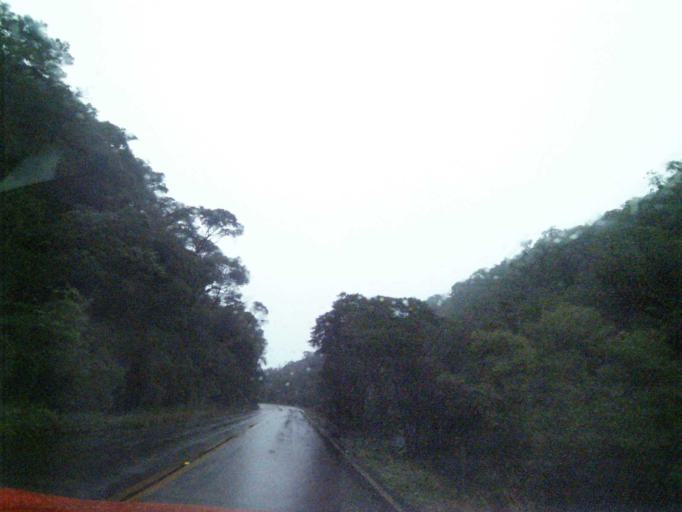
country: BR
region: Santa Catarina
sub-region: Anitapolis
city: Anitapolis
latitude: -27.7659
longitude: -49.0394
